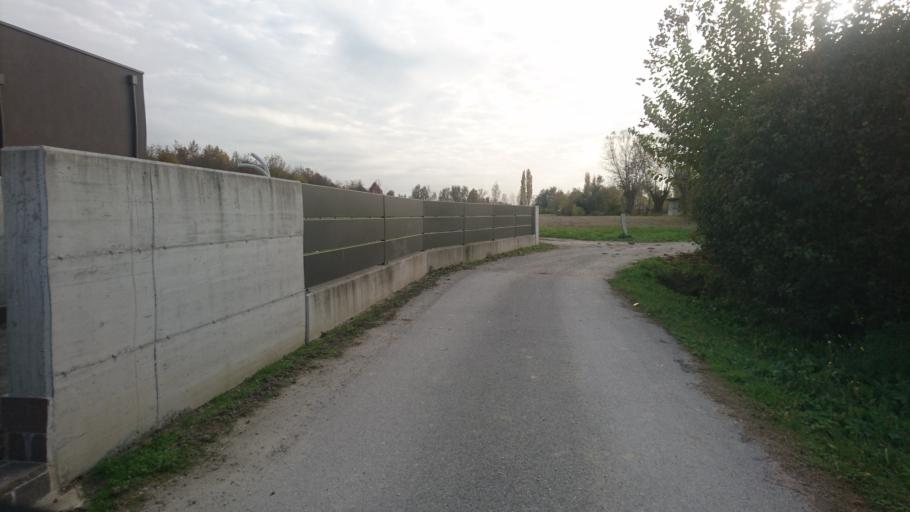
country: IT
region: Veneto
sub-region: Provincia di Padova
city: Mandriola-Sant'Agostino
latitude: 45.3816
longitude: 11.8365
